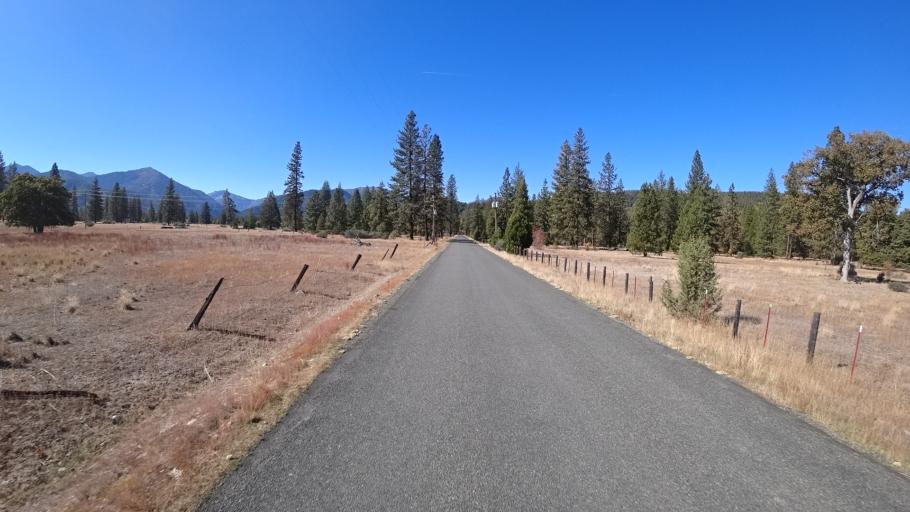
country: US
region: California
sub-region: Siskiyou County
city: Yreka
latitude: 41.5485
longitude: -122.9269
